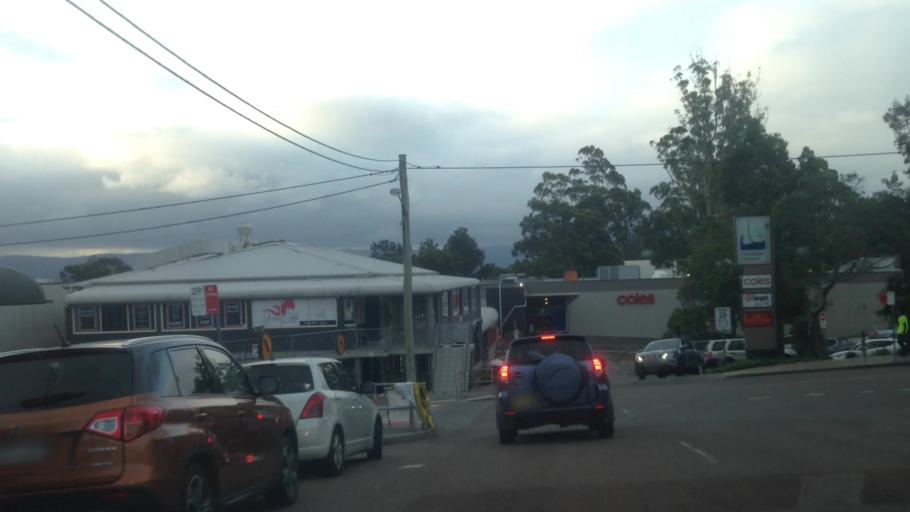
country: AU
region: New South Wales
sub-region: Lake Macquarie Shire
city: Dora Creek
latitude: -33.1074
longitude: 151.4886
